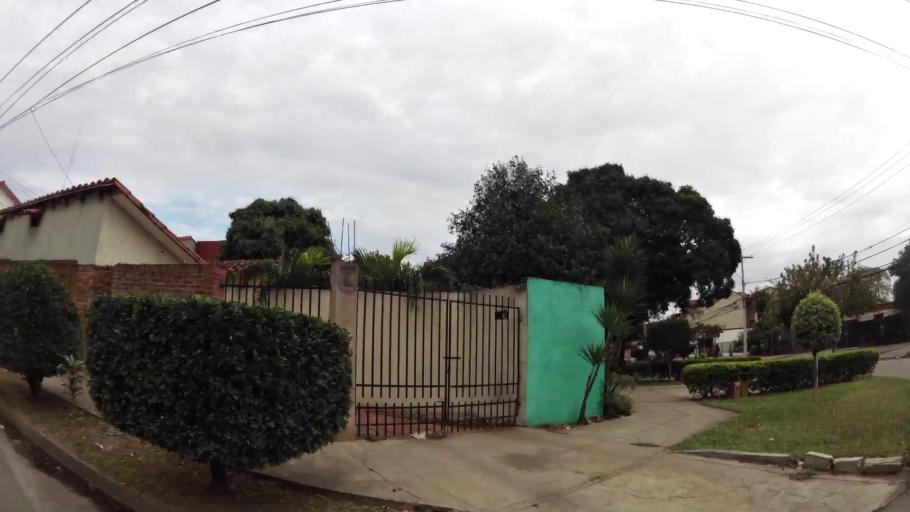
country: BO
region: Santa Cruz
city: Santa Cruz de la Sierra
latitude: -17.7586
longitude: -63.1615
